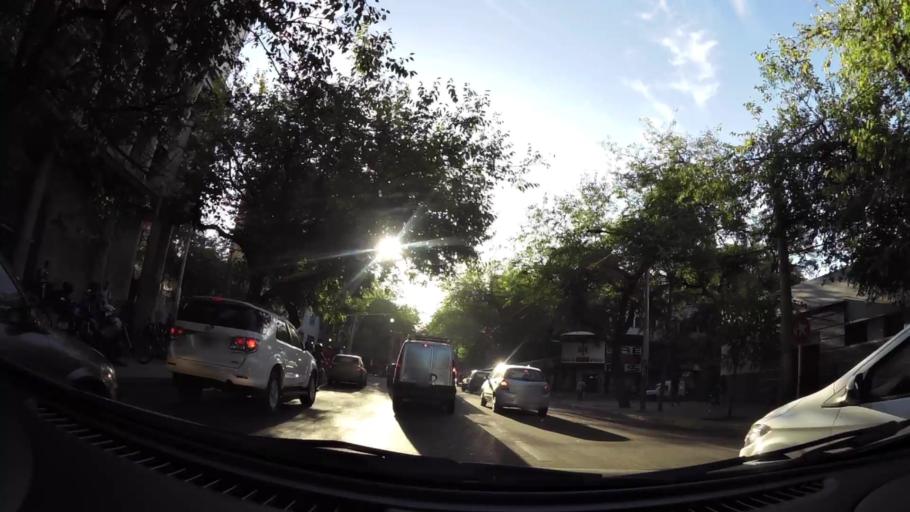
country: AR
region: Mendoza
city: Mendoza
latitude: -32.8948
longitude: -68.8415
